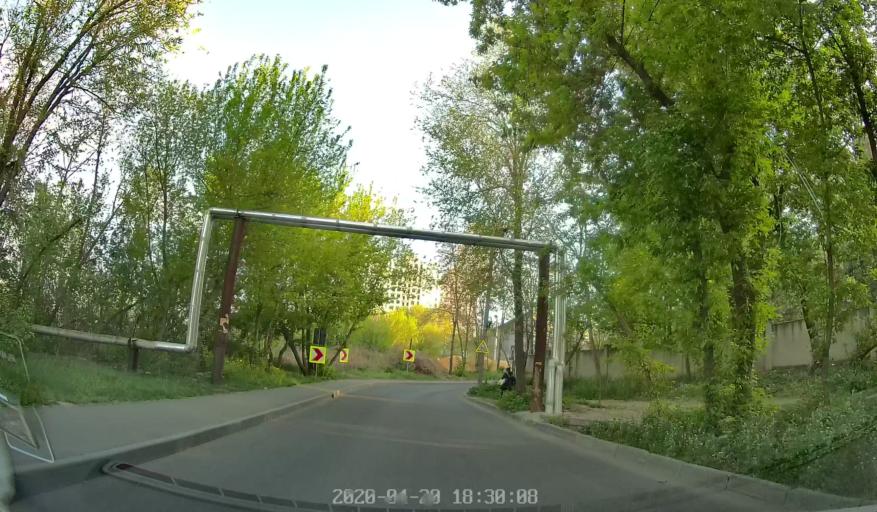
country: MD
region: Chisinau
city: Chisinau
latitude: 46.9894
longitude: 28.8352
